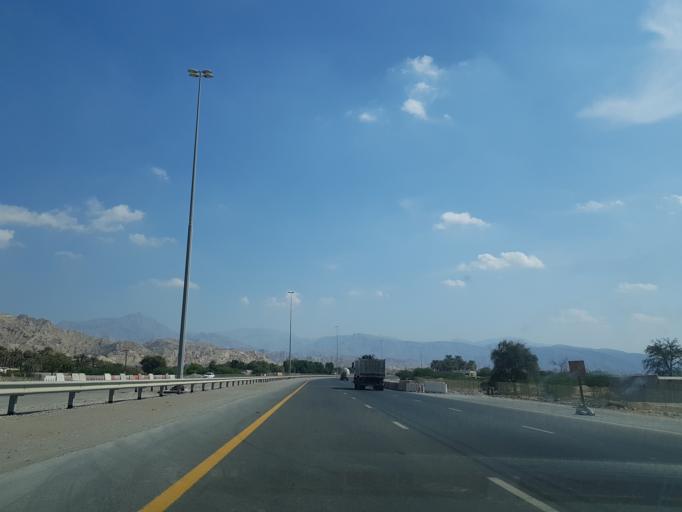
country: AE
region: Ra's al Khaymah
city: Ras al-Khaimah
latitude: 25.8272
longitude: 56.0199
